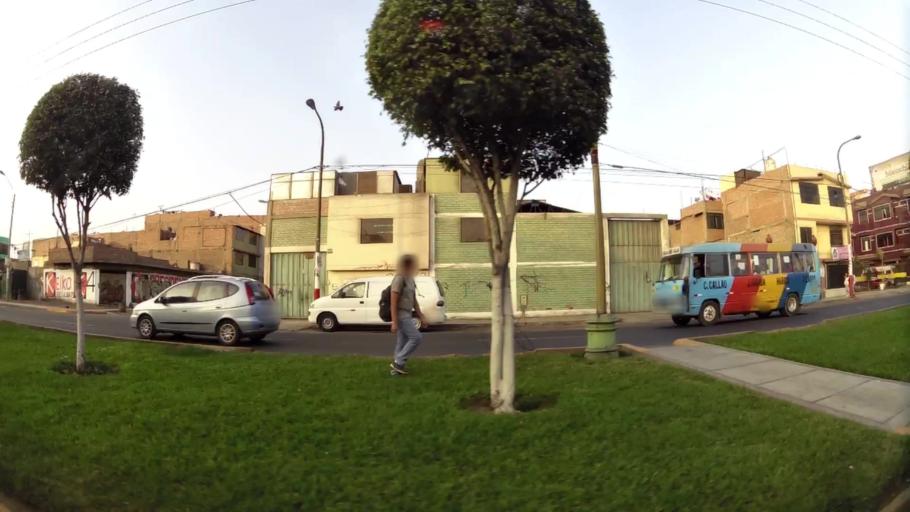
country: PE
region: Callao
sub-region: Callao
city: Callao
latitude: -12.0038
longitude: -77.1048
